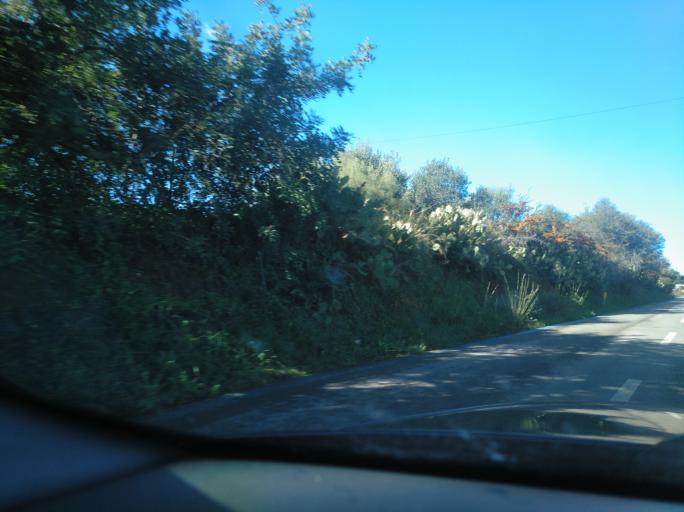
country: PT
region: Faro
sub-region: Vila Real de Santo Antonio
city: Monte Gordo
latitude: 37.1682
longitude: -7.5366
